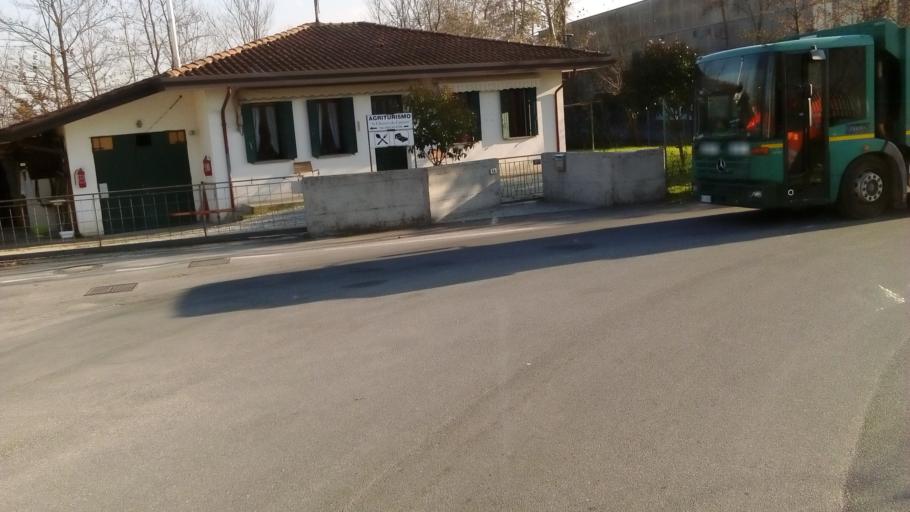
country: IT
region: Veneto
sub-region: Provincia di Treviso
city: Oderzo
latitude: 45.8052
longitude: 12.5013
